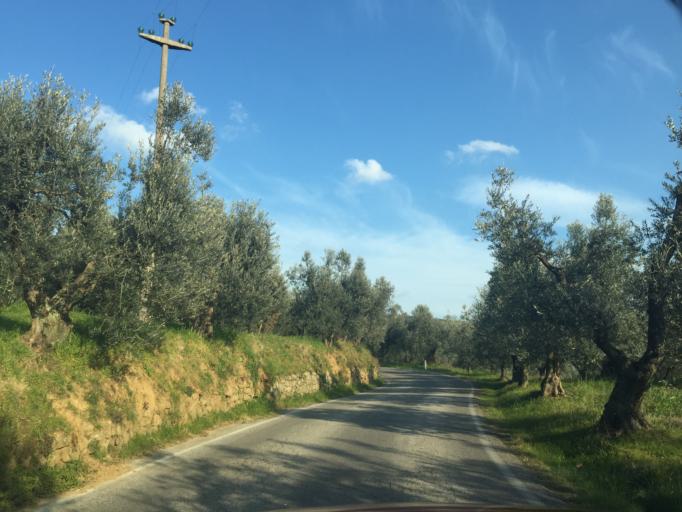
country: IT
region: Tuscany
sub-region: Province of Florence
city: Vinci
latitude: 43.7979
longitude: 10.9325
